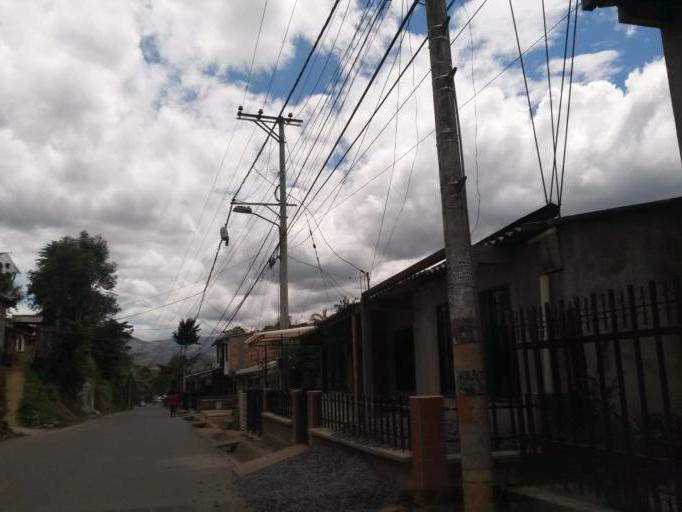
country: CO
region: Cauca
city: Popayan
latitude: 2.4804
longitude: -76.5689
